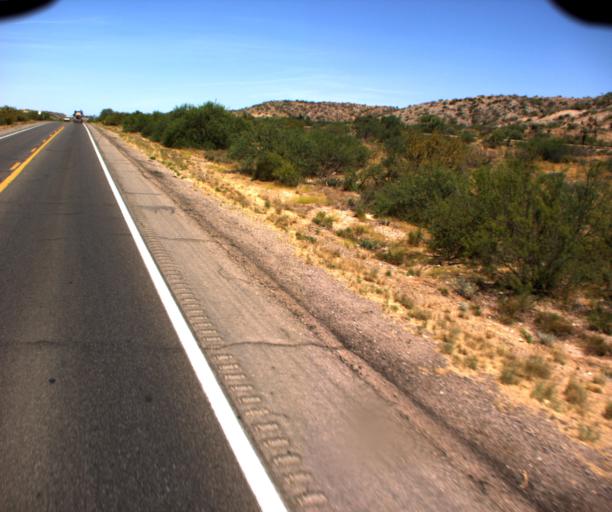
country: US
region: Arizona
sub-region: Gila County
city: Globe
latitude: 33.3679
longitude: -110.7209
